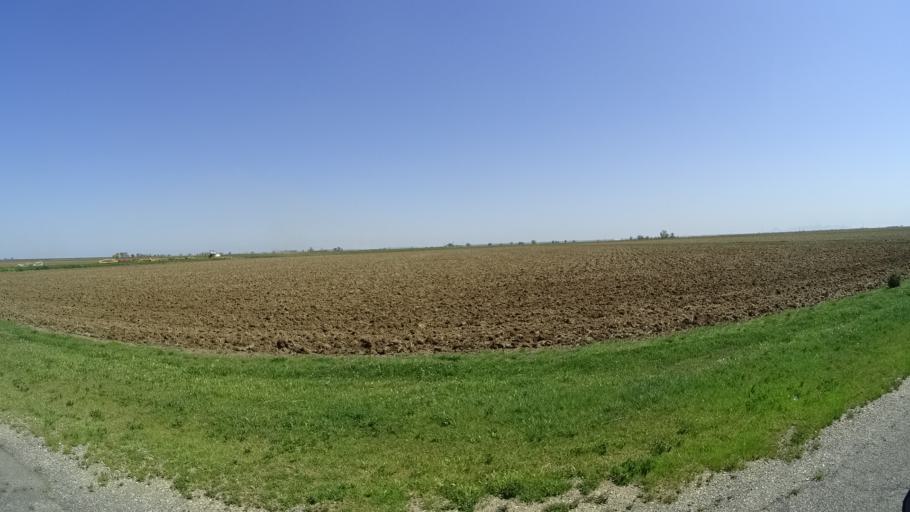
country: US
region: California
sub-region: Glenn County
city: Willows
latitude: 39.4931
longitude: -122.1263
